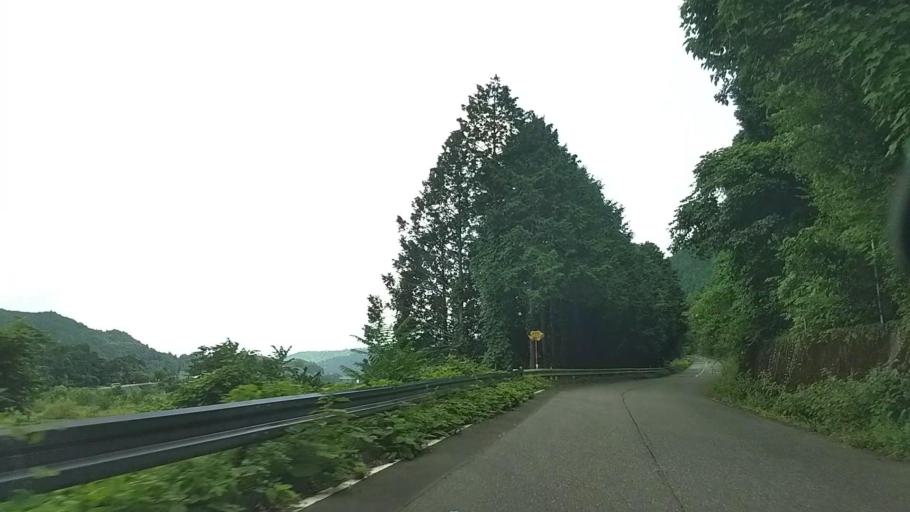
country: JP
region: Shizuoka
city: Fujinomiya
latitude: 35.2147
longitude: 138.5395
